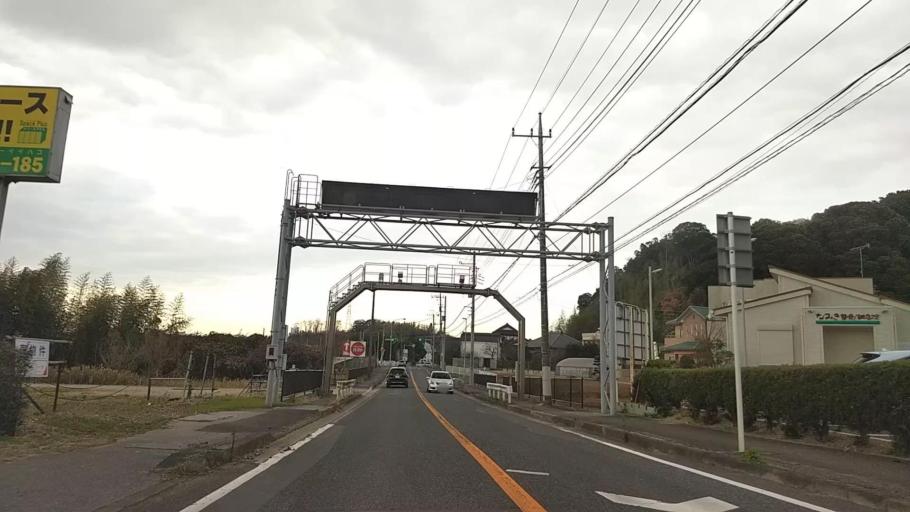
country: JP
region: Chiba
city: Chiba
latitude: 35.6085
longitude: 140.1617
